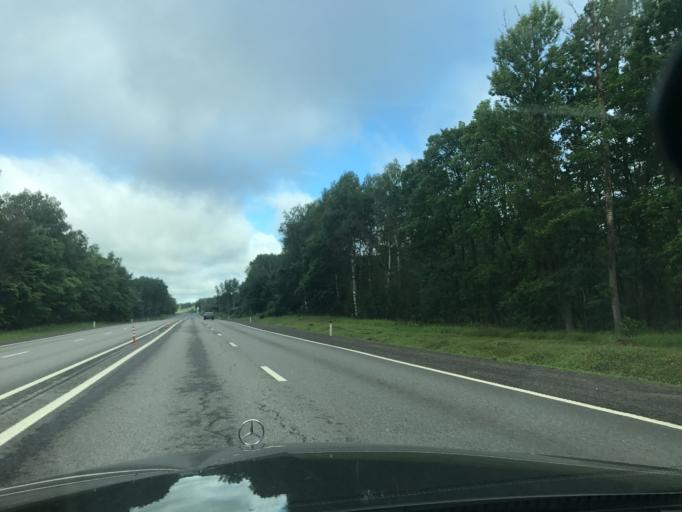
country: RU
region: Smolensk
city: Gagarin
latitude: 55.4995
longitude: 35.2297
